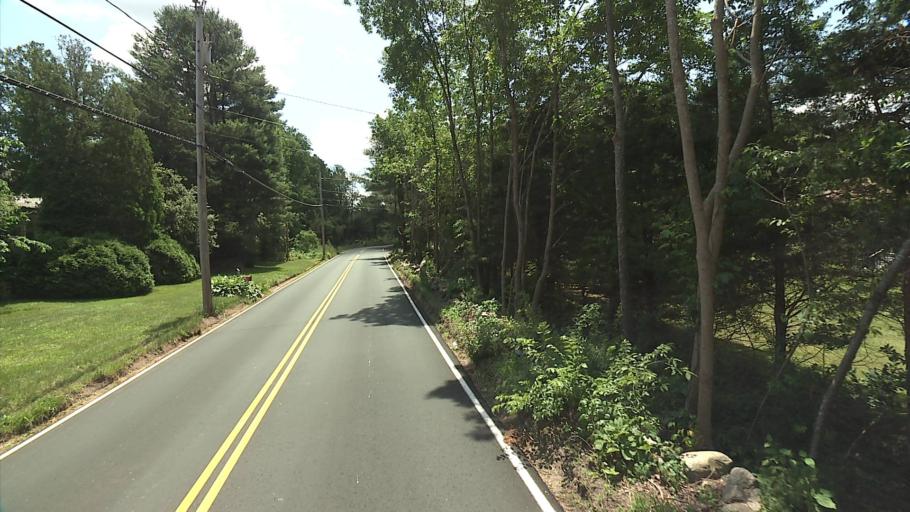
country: US
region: Connecticut
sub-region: New London County
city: Preston City
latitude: 41.5701
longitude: -71.8925
